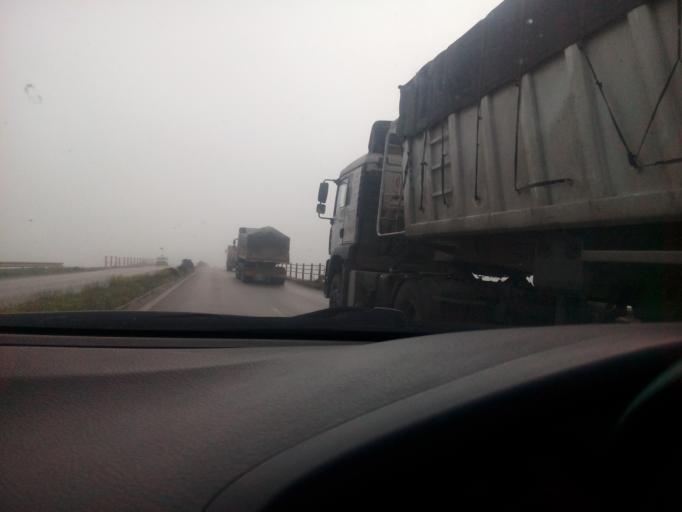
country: DZ
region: Oran
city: Es Senia
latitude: 35.6056
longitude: -0.7392
